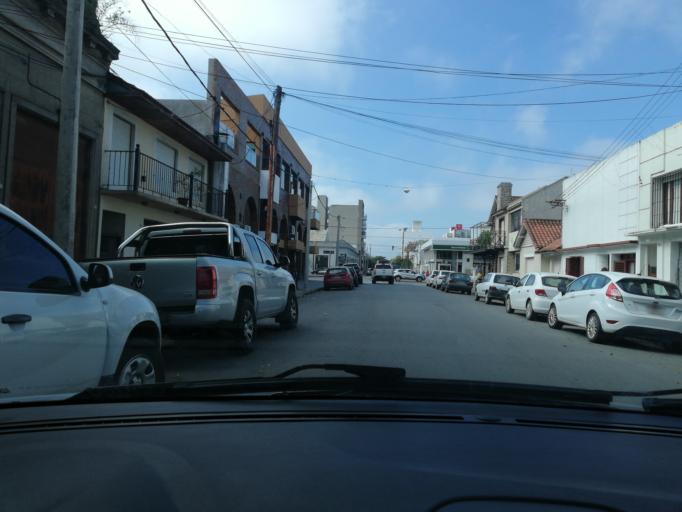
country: AR
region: Buenos Aires
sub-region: Partido de Balcarce
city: Balcarce
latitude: -37.8443
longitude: -58.2542
